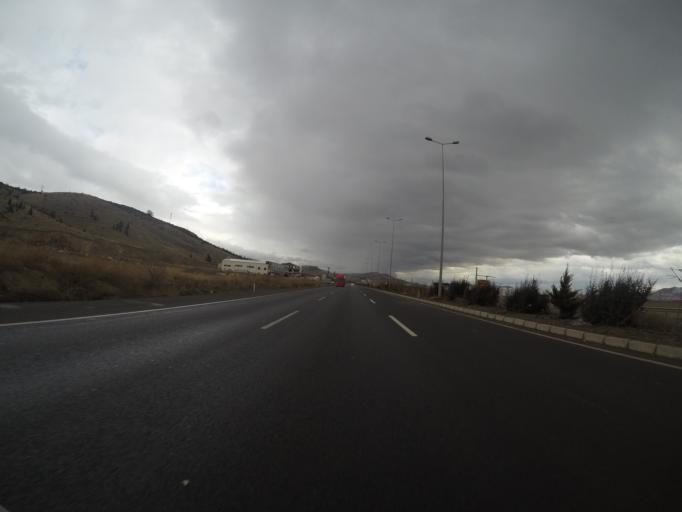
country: TR
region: Kayseri
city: Melikgazi
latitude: 38.7453
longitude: 35.3020
